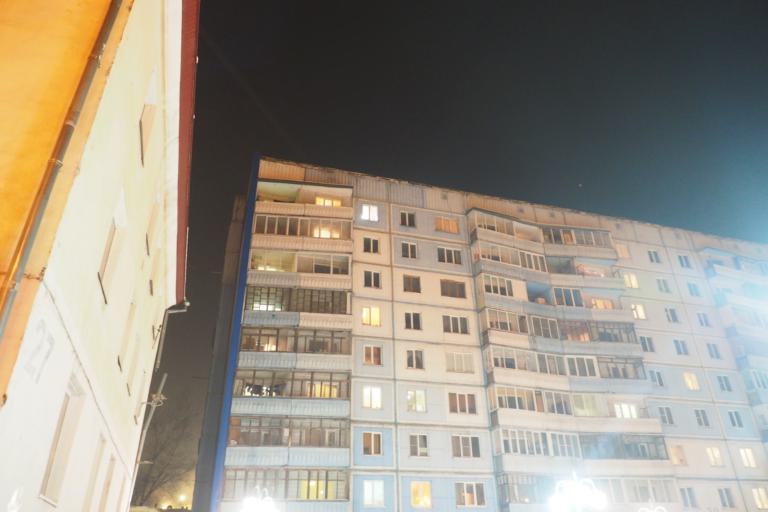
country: RU
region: Altay
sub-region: Mayminskiy Rayon
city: Gorno-Altaysk
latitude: 51.9587
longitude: 85.9537
